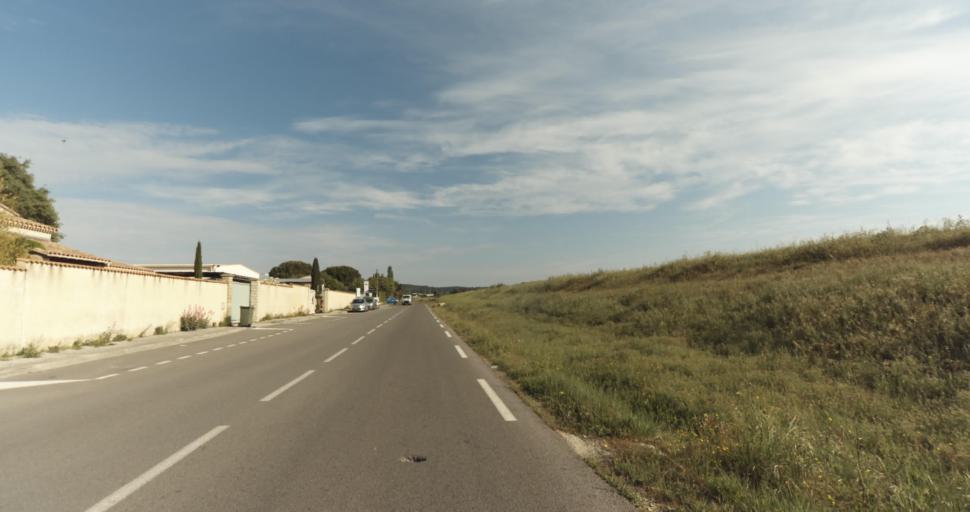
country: FR
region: Languedoc-Roussillon
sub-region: Departement du Gard
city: Rodilhan
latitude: 43.8503
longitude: 4.4086
